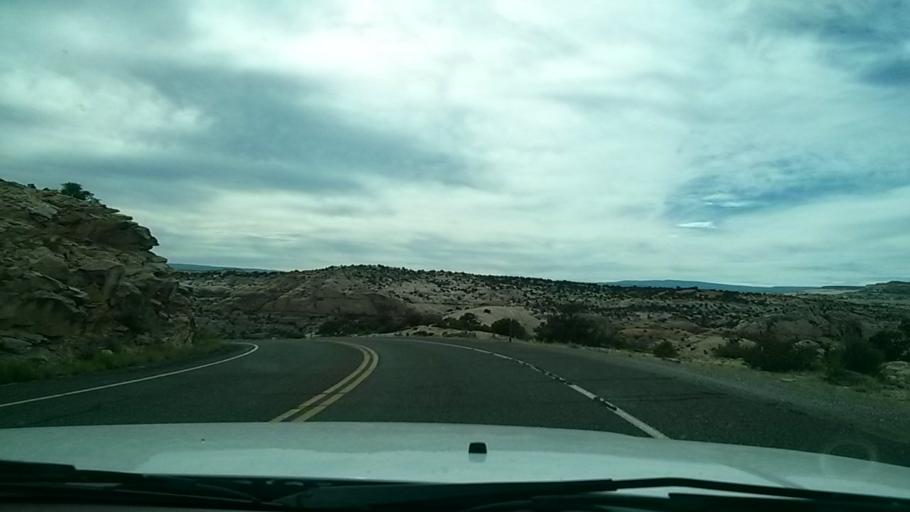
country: US
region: Utah
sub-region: Wayne County
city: Loa
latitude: 37.8035
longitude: -111.4025
